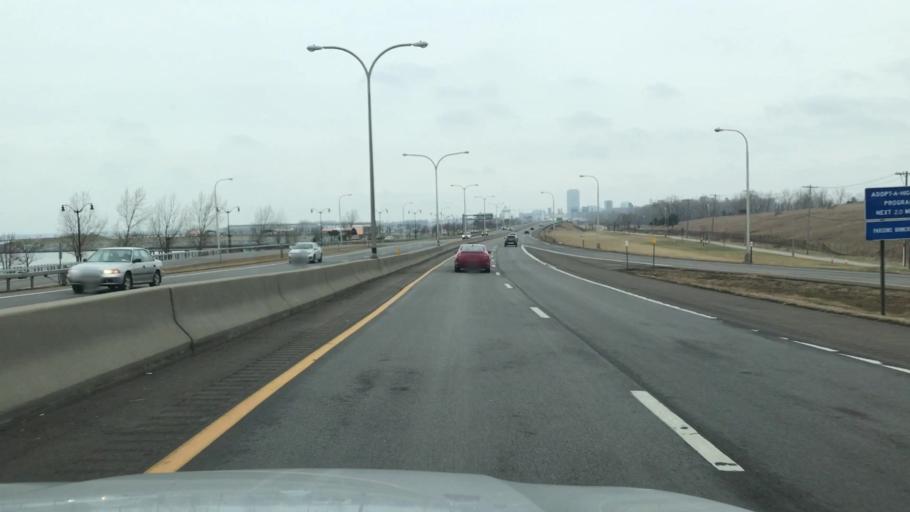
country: US
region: New York
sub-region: Erie County
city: Lackawanna
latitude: 42.8410
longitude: -78.8578
